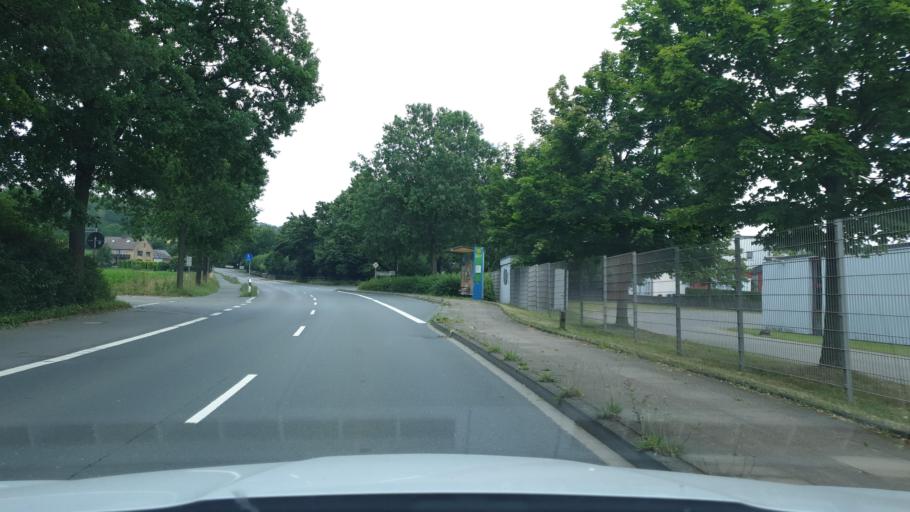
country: DE
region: North Rhine-Westphalia
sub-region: Regierungsbezirk Detmold
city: Bad Salzuflen
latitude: 52.1335
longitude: 8.7906
